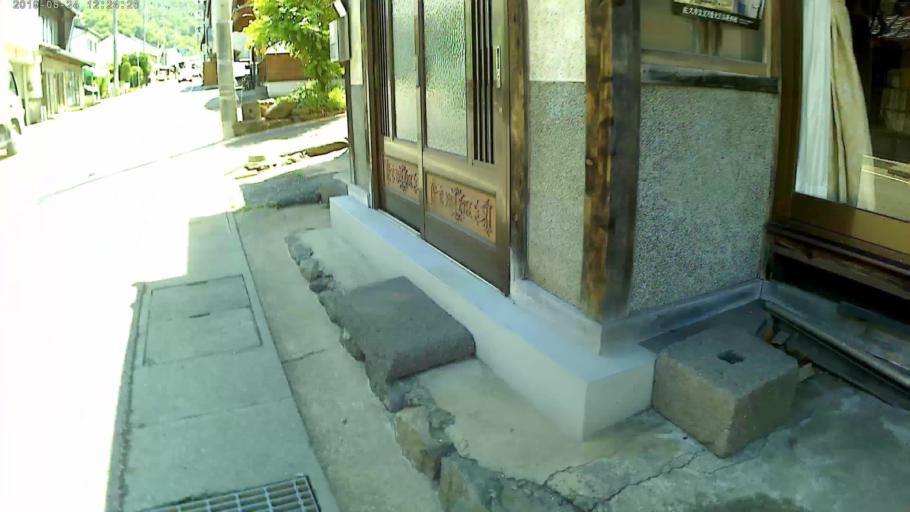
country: JP
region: Nagano
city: Komoro
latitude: 36.2643
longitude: 138.3636
